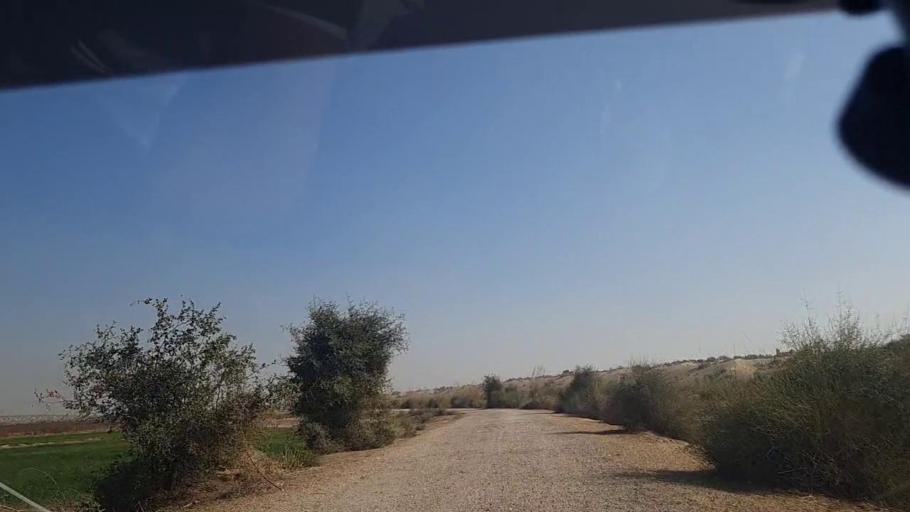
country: PK
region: Sindh
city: Khanpur
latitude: 27.5590
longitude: 69.3269
